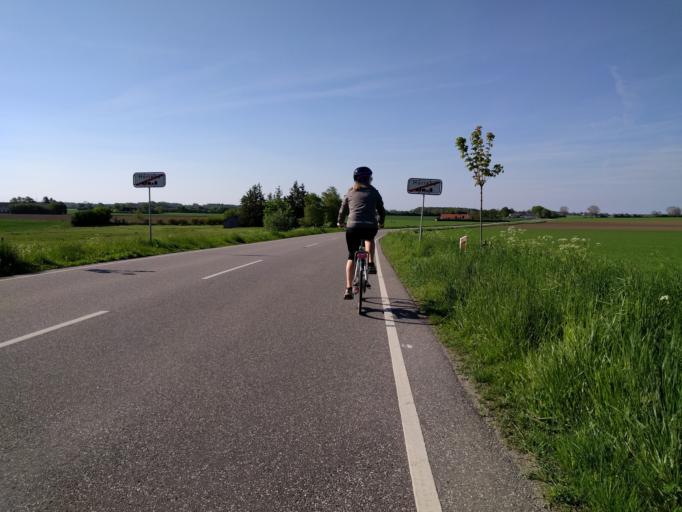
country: DK
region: Zealand
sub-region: Guldborgsund Kommune
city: Stubbekobing
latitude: 54.7973
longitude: 11.9928
